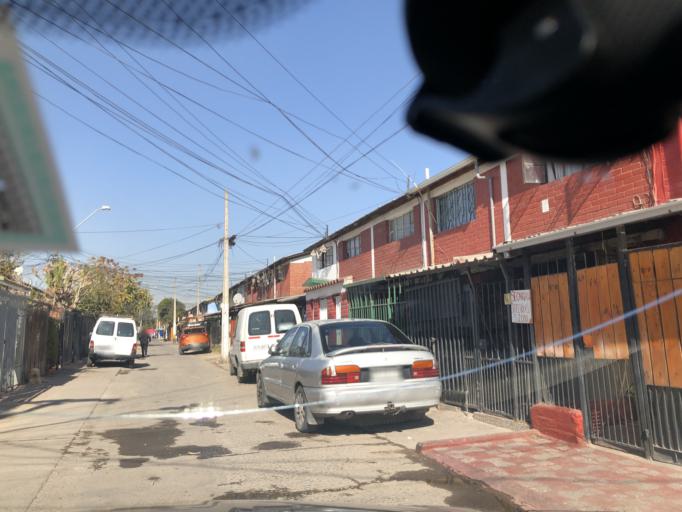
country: CL
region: Santiago Metropolitan
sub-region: Provincia de Santiago
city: La Pintana
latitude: -33.5867
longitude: -70.6008
